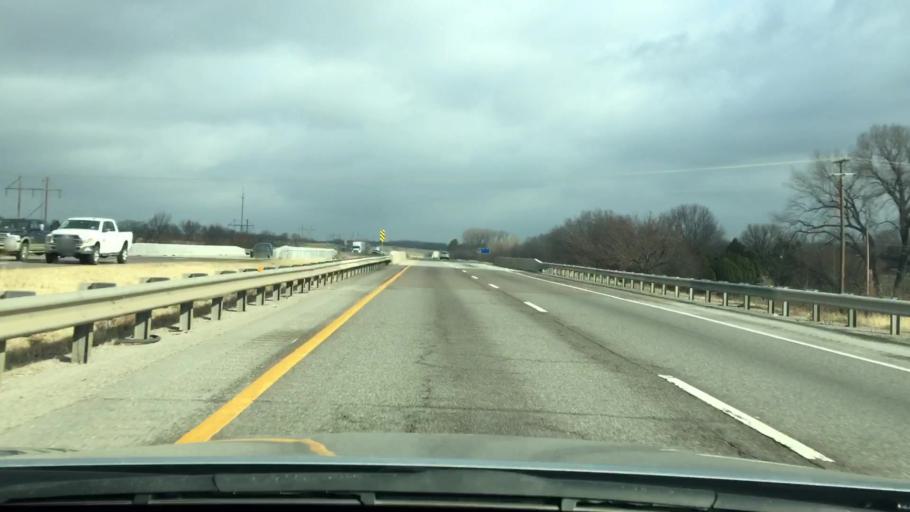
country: US
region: Oklahoma
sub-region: McClain County
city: Purcell
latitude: 35.0290
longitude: -97.3758
